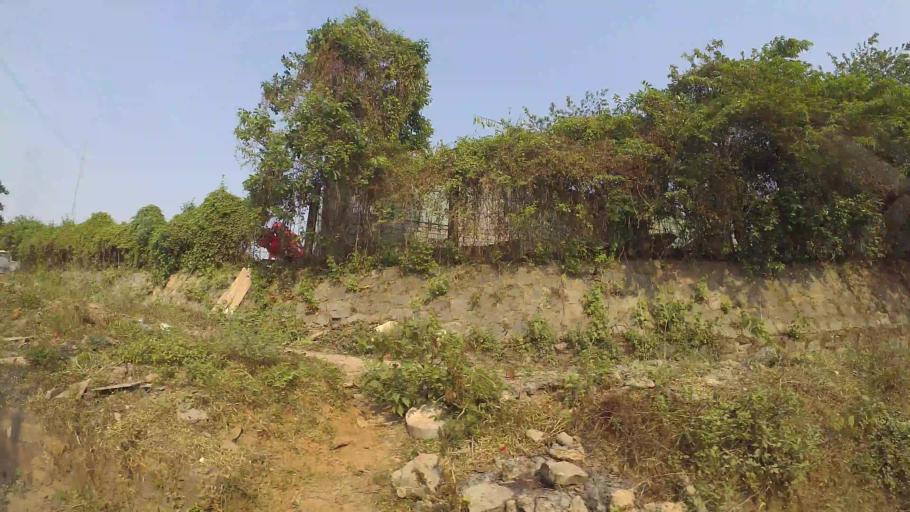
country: VN
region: Da Nang
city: Cam Le
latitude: 16.0135
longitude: 108.1866
